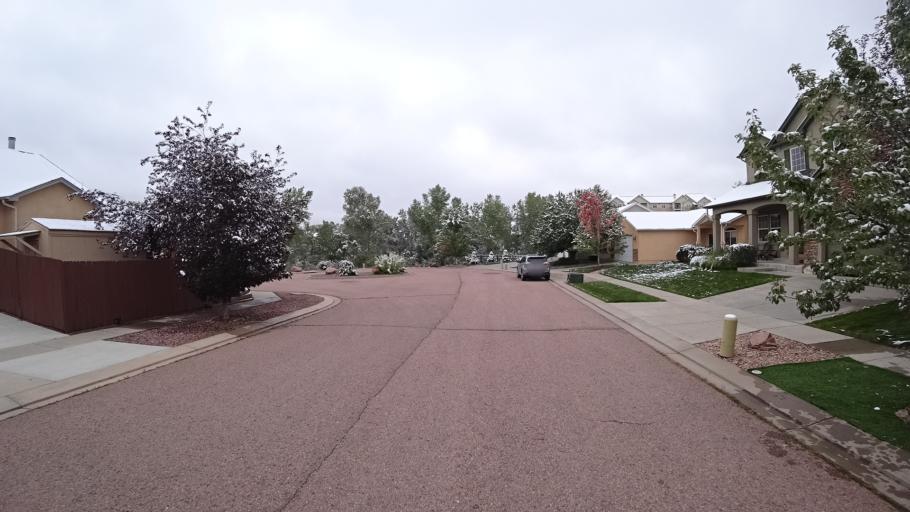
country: US
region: Colorado
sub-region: El Paso County
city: Colorado Springs
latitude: 38.9305
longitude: -104.7791
